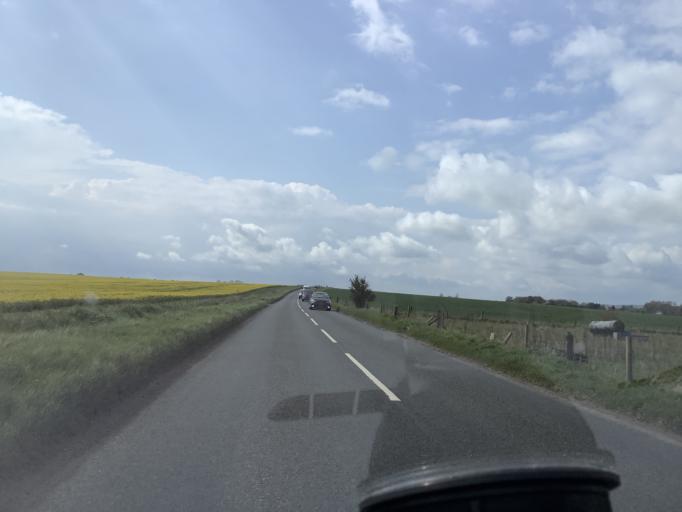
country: GB
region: England
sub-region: Borough of Swindon
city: Wroughton
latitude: 51.4795
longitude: -1.8435
